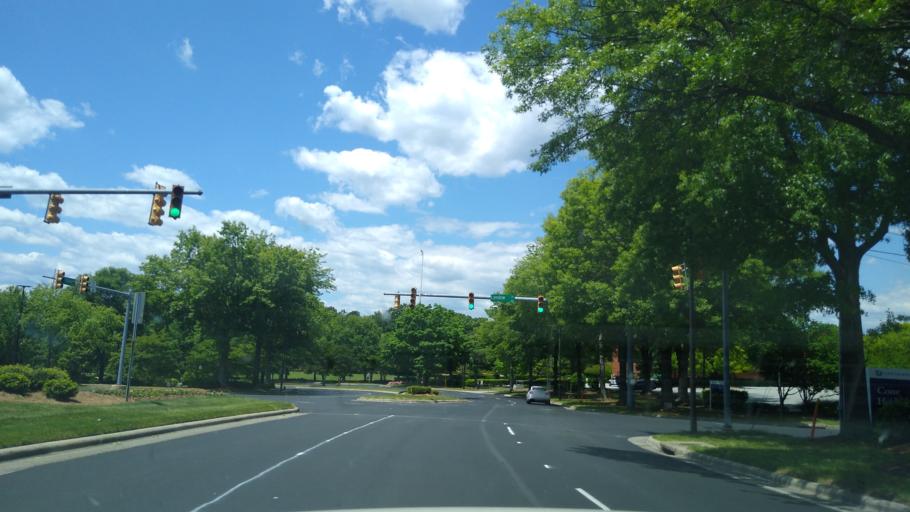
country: US
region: North Carolina
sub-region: Guilford County
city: Greensboro
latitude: 36.0920
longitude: -79.8190
